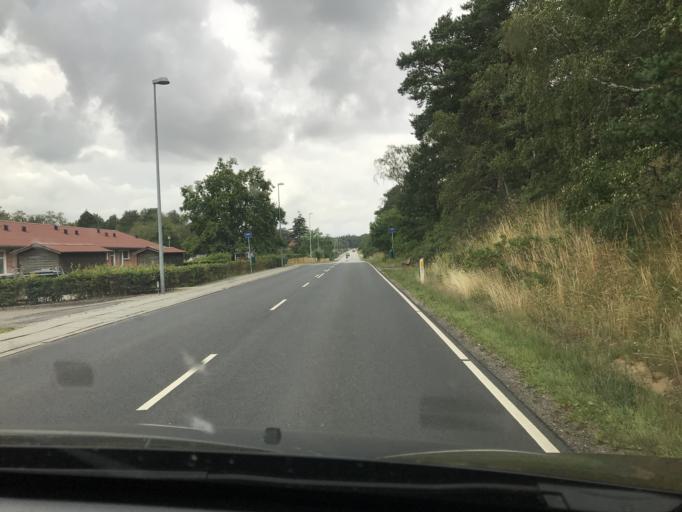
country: DK
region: Central Jutland
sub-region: Norddjurs Kommune
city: Auning
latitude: 56.3950
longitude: 10.4105
